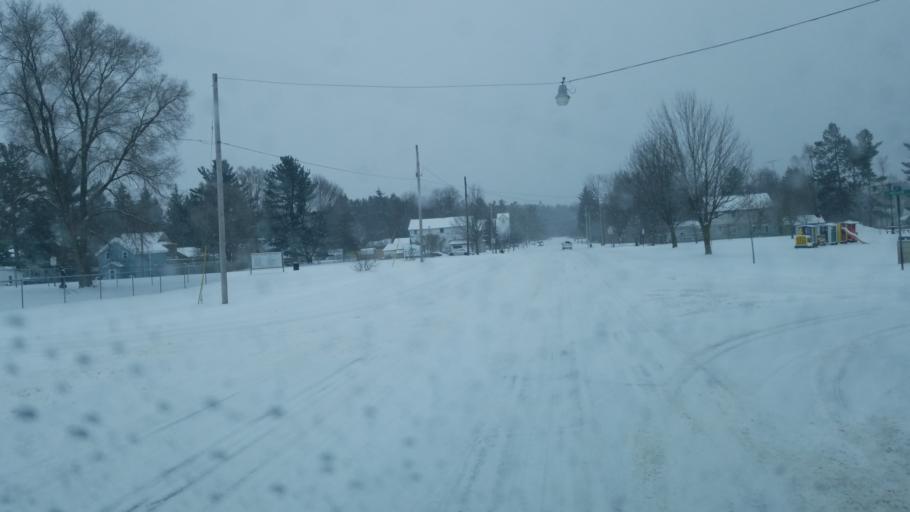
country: US
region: Michigan
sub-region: Osceola County
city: Evart
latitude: 43.8999
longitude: -85.2594
